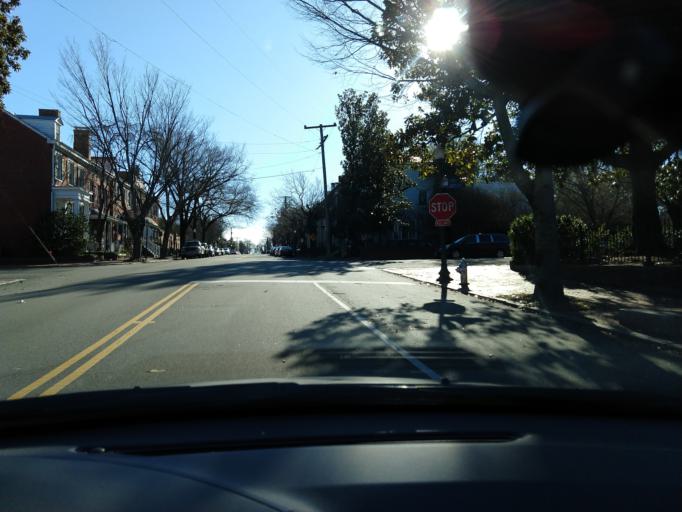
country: US
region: Virginia
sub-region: Henrico County
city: Montrose
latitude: 37.5328
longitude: -77.4209
